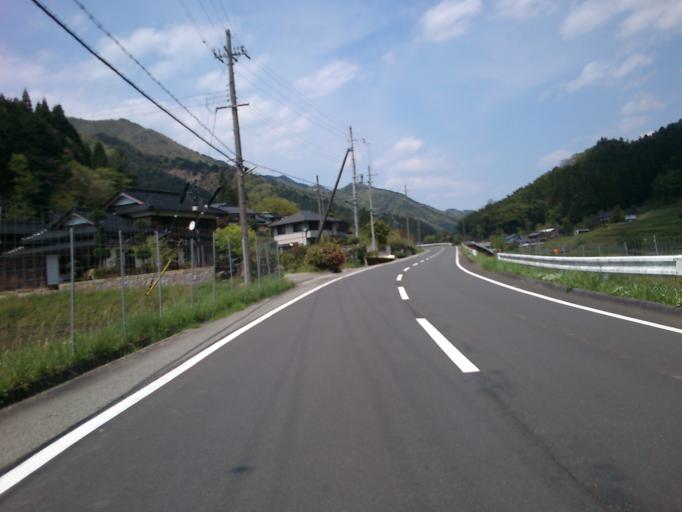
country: JP
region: Kyoto
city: Fukuchiyama
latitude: 35.3719
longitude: 134.9384
